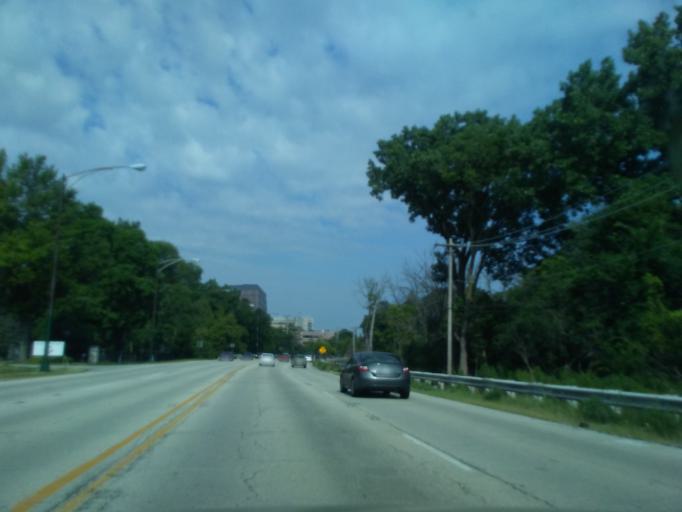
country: US
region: Illinois
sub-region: Cook County
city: Park Ridge
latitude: 41.9886
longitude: -87.8529
